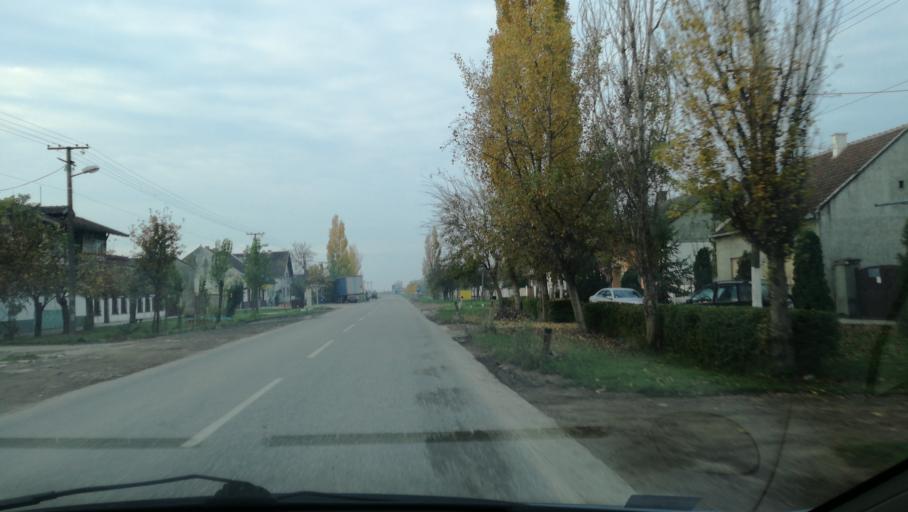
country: RS
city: Basaid
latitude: 45.6382
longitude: 20.4121
